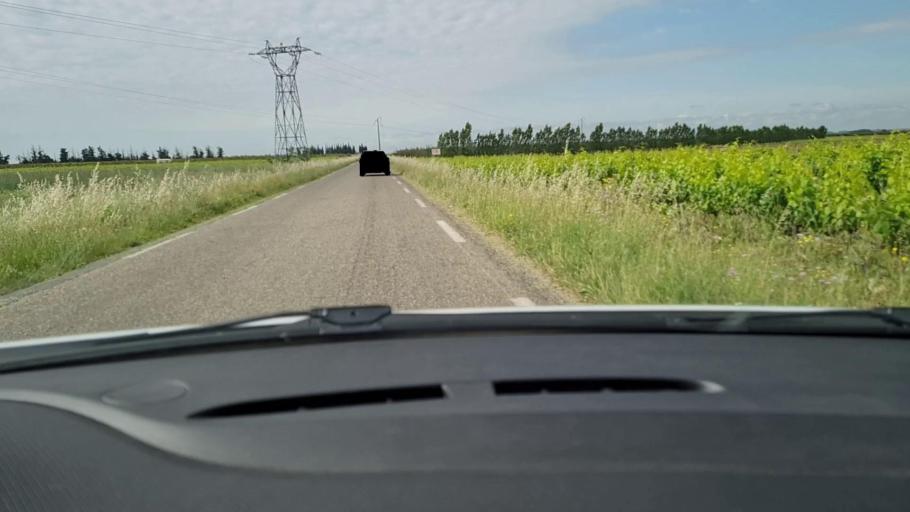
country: FR
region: Languedoc-Roussillon
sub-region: Departement du Gard
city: Bellegarde
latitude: 43.7782
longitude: 4.5210
